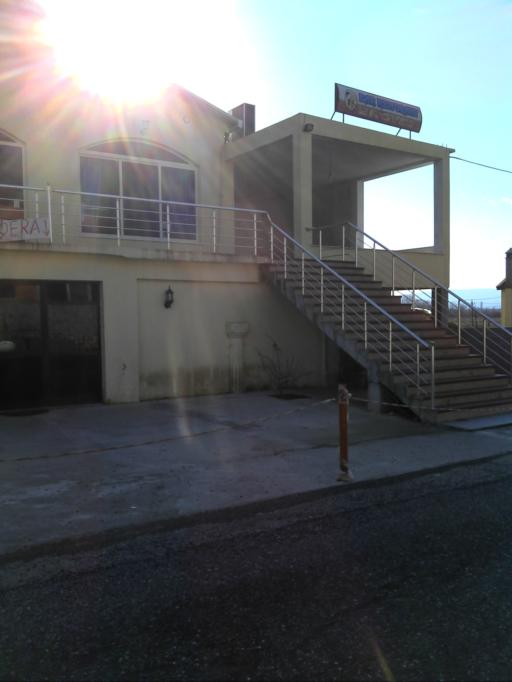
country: AL
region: Shkoder
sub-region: Rrethi i Shkodres
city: Dajc
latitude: 42.0116
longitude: 19.4119
